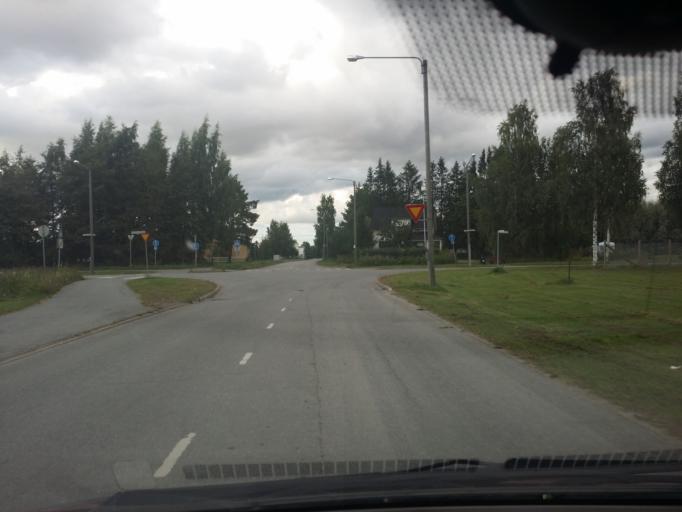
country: FI
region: Satakunta
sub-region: Pori
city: Pori
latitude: 61.5049
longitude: 21.8046
